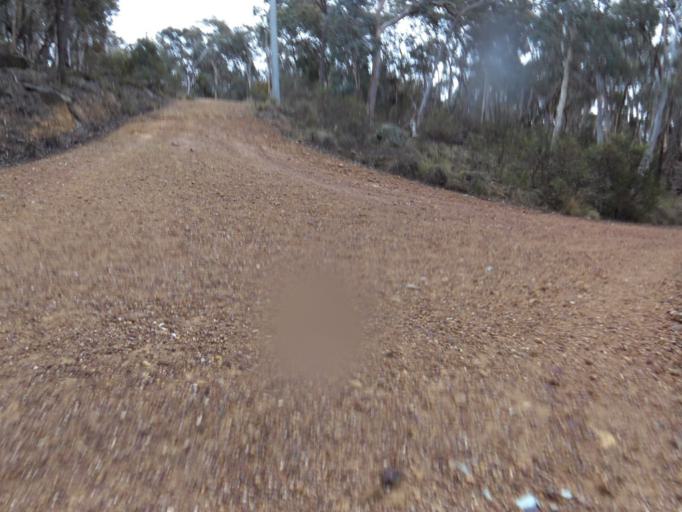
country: AU
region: Australian Capital Territory
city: Acton
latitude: -35.2692
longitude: 149.0989
